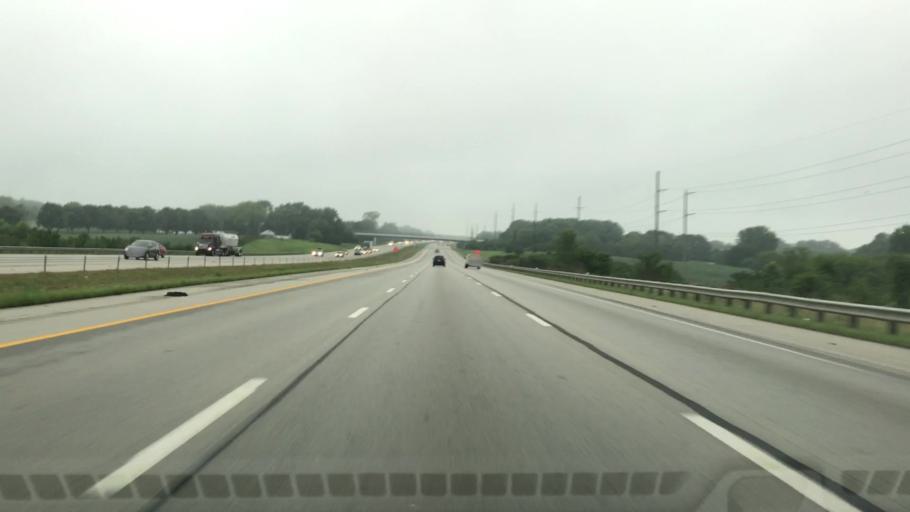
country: US
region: Ohio
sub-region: Clark County
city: Springfield
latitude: 39.8907
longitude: -83.7665
